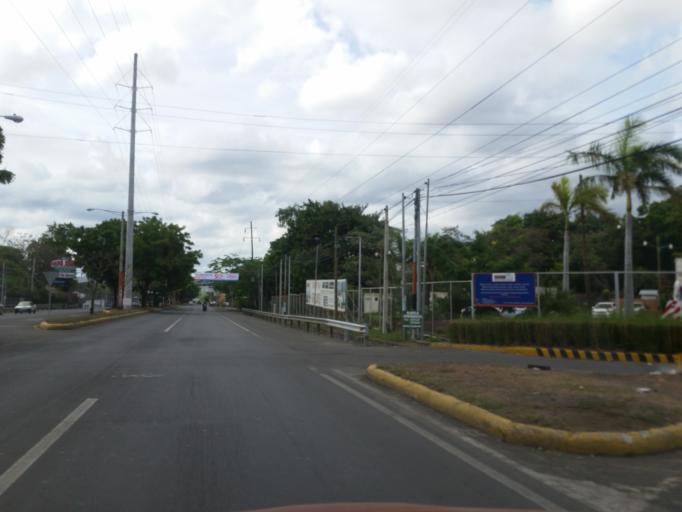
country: NI
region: Masaya
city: Ticuantepe
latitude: 12.0654
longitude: -86.2119
